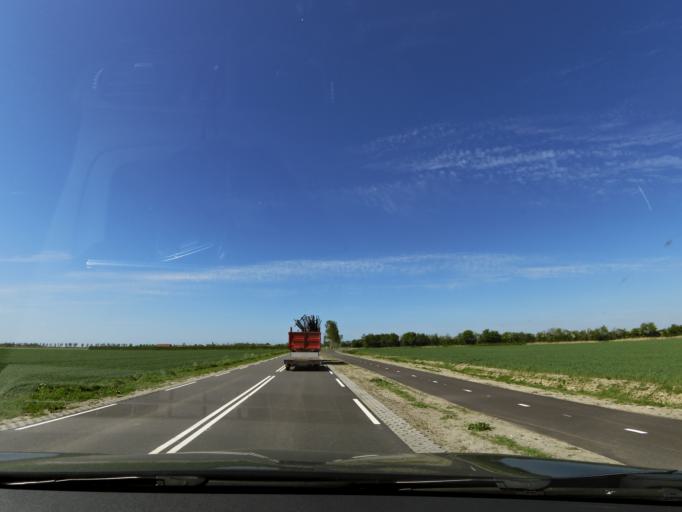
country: NL
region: Zeeland
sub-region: Schouwen-Duiveland
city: Bruinisse
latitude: 51.6754
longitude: 3.9869
